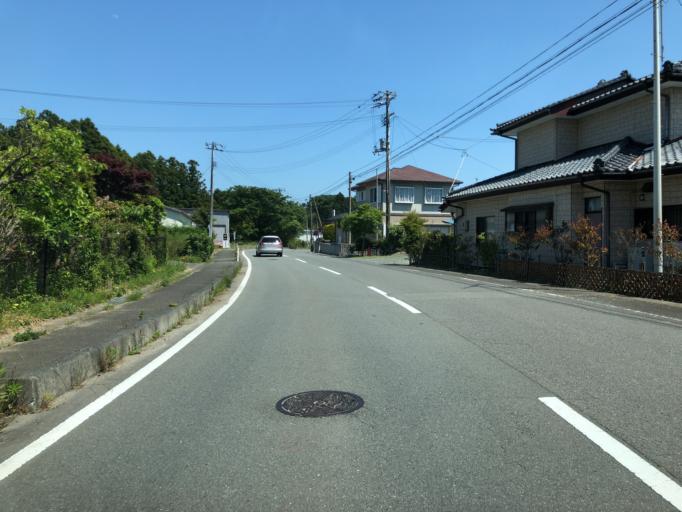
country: JP
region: Fukushima
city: Iwaki
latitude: 37.2257
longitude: 141.0004
